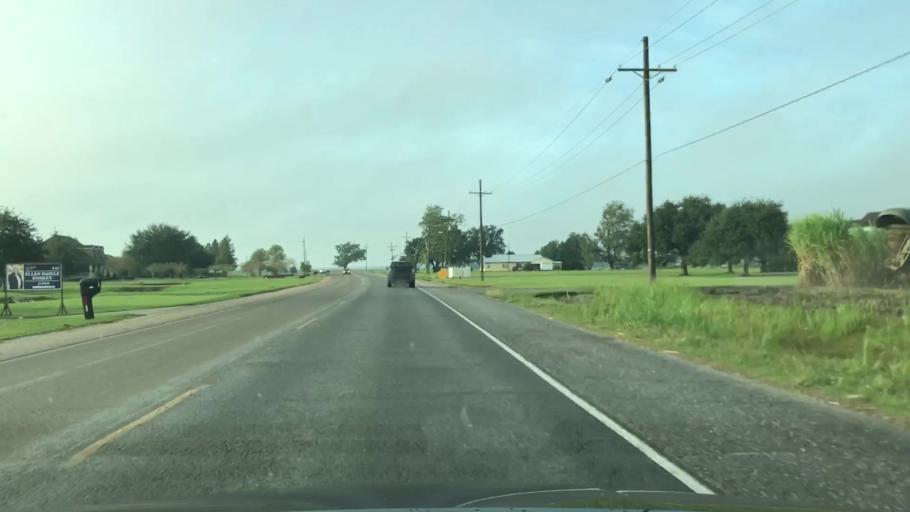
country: US
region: Louisiana
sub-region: Terrebonne Parish
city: Gray
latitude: 29.6659
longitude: -90.8190
